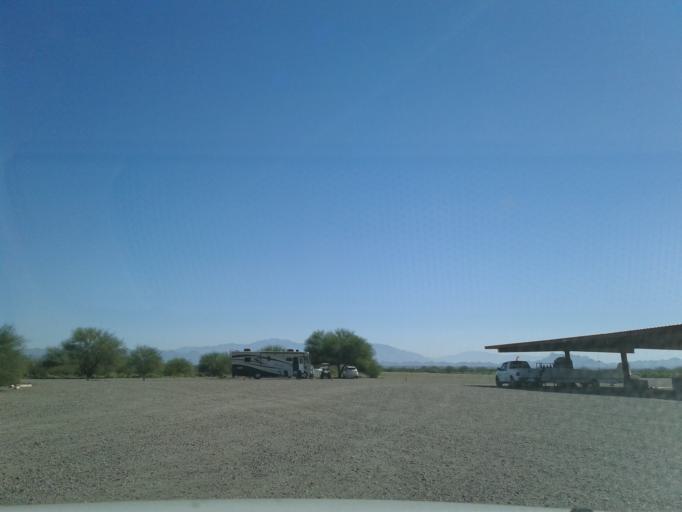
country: US
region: Arizona
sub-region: Pima County
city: Avra Valley
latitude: 32.4295
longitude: -111.3868
